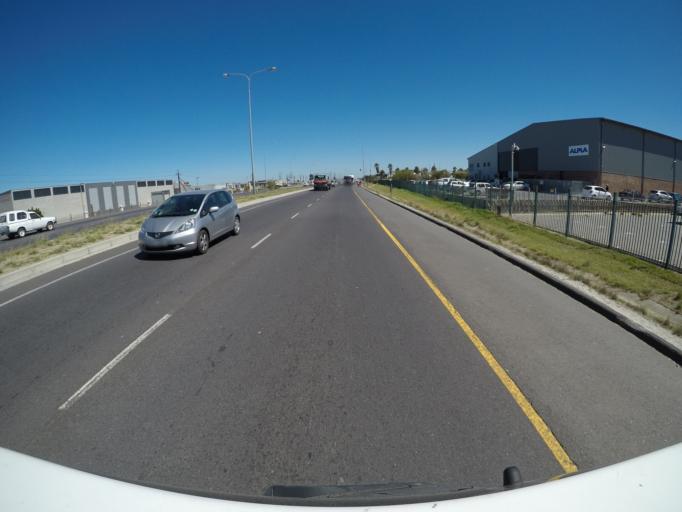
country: ZA
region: Western Cape
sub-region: Overberg District Municipality
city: Grabouw
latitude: -34.1045
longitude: 18.8557
